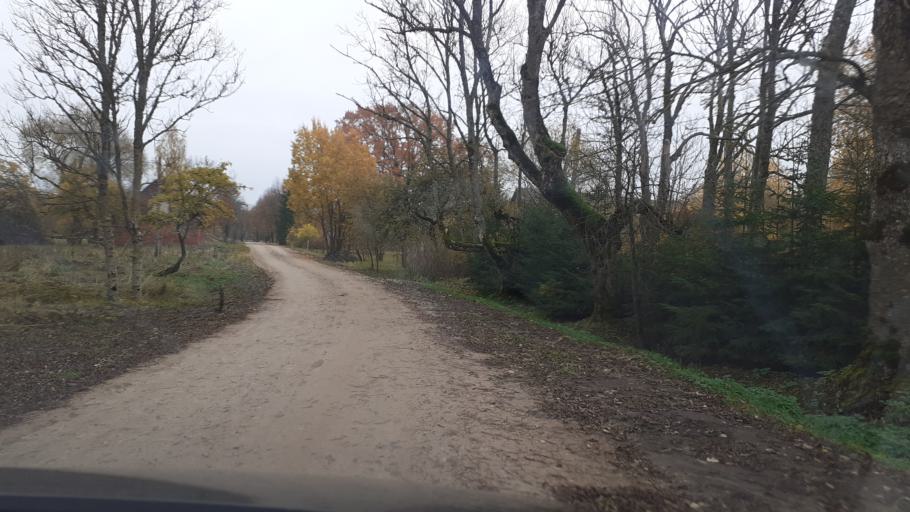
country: LV
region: Skrunda
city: Skrunda
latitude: 56.8564
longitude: 22.2231
